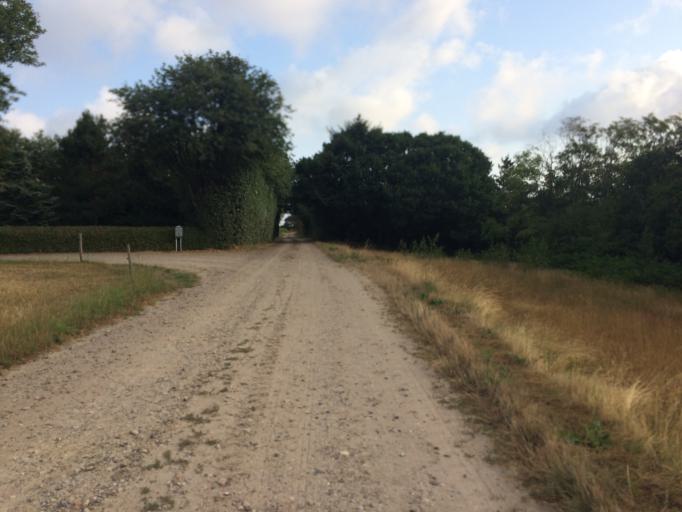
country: DK
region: Central Jutland
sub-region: Holstebro Kommune
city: Vinderup
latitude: 56.6140
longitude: 8.7155
